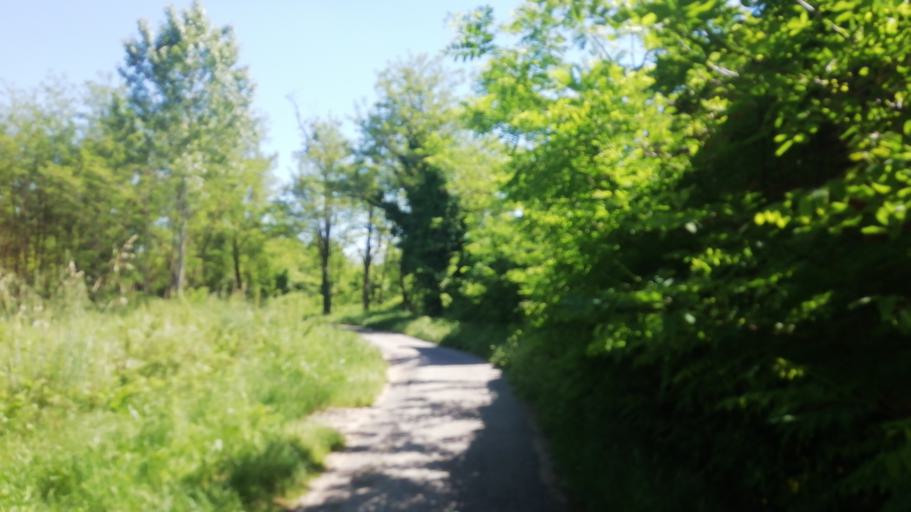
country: IT
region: Emilia-Romagna
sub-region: Provincia di Piacenza
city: Borgonovo Valtidone
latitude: 45.0076
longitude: 9.4463
